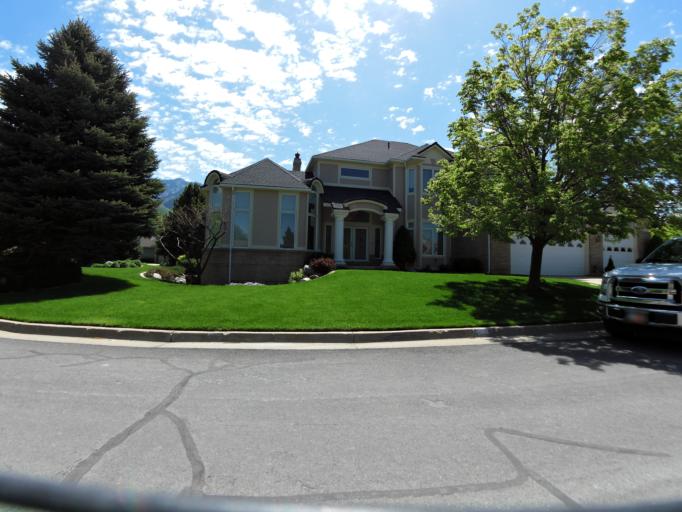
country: US
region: Utah
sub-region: Weber County
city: Uintah
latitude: 41.1760
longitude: -111.9368
